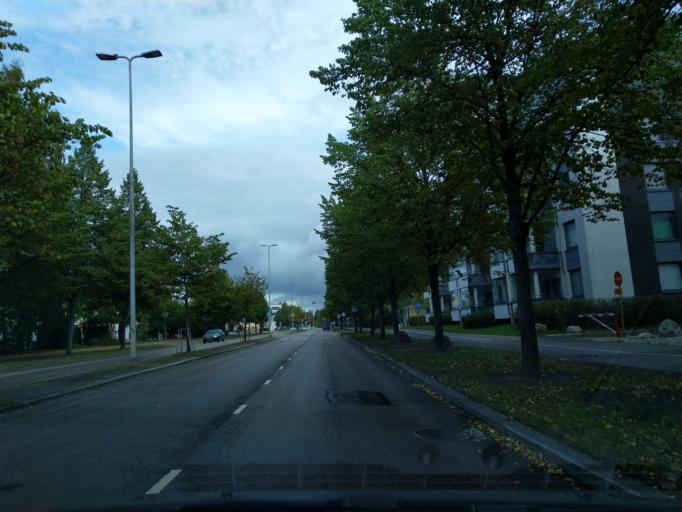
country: FI
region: Uusimaa
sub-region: Helsinki
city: Vantaa
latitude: 60.2915
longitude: 25.0315
